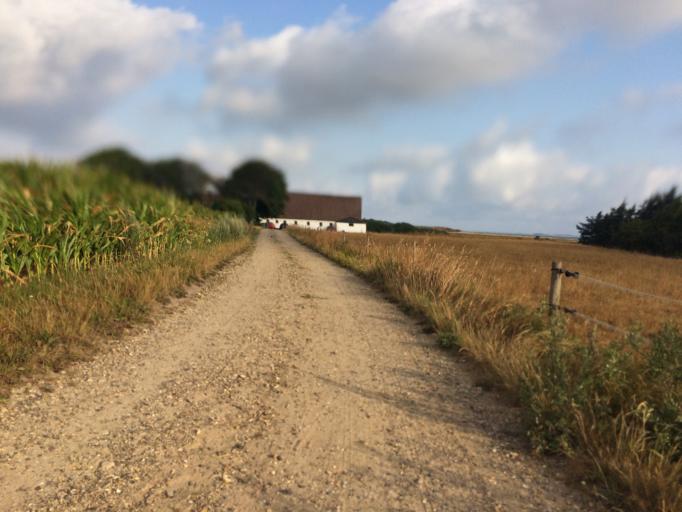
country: DK
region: Central Jutland
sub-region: Holstebro Kommune
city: Vinderup
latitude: 56.6164
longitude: 8.7151
